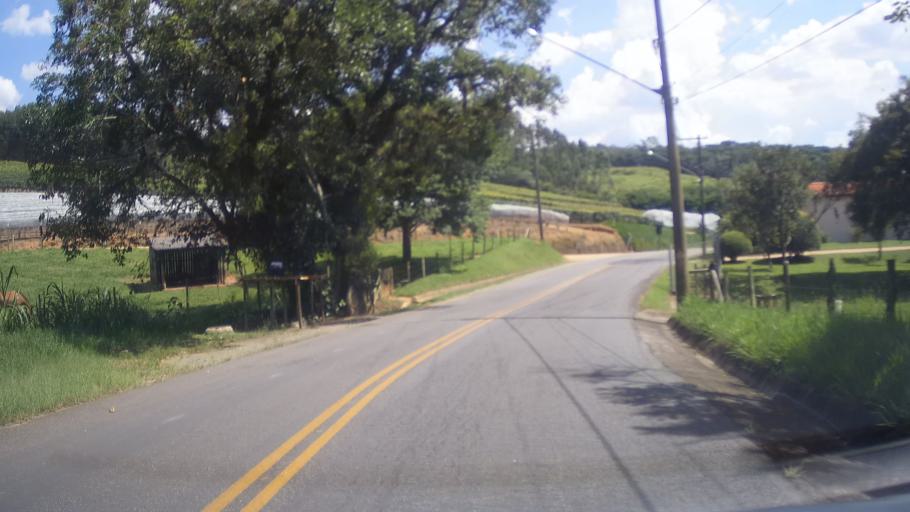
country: BR
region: Sao Paulo
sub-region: Varzea Paulista
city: Varzea Paulista
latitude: -23.1284
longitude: -46.8229
